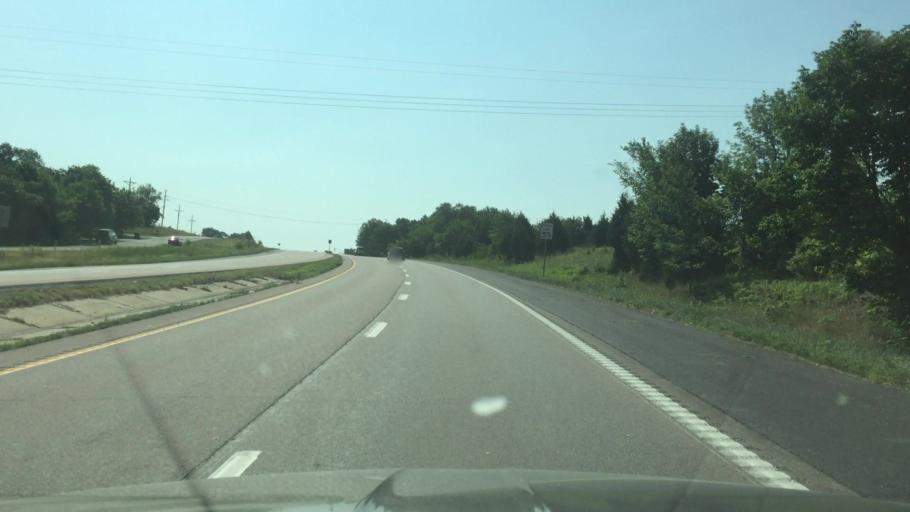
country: US
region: Missouri
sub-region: Pettis County
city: Sedalia
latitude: 38.7204
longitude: -93.2982
